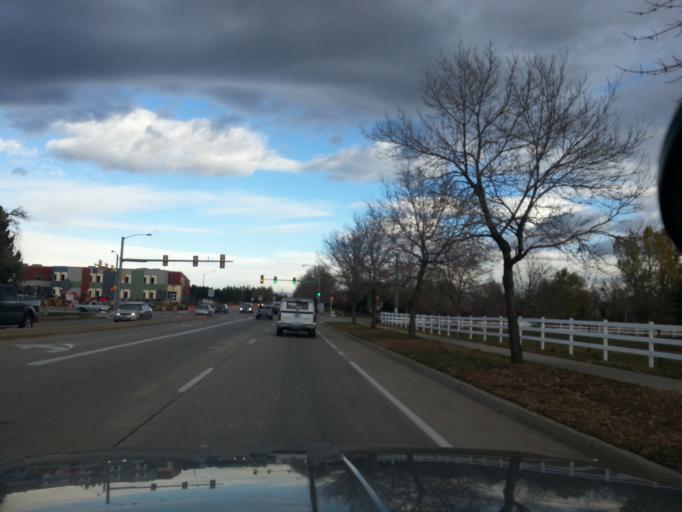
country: US
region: Colorado
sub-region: Larimer County
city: Fort Collins
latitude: 40.5374
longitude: -105.1151
